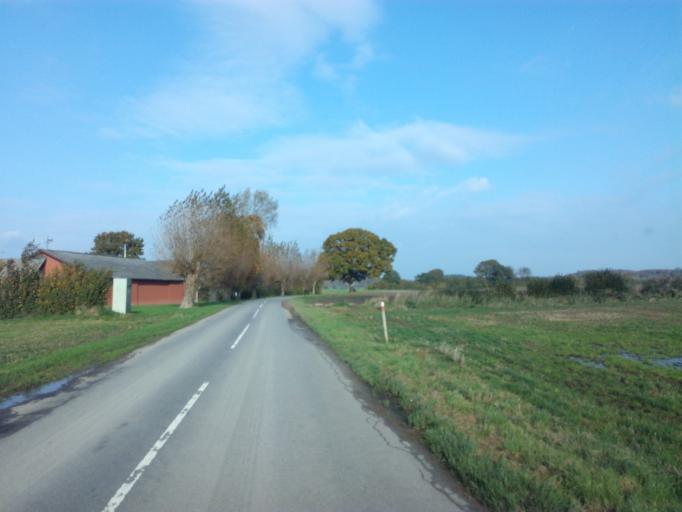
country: DK
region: South Denmark
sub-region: Vejle Kommune
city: Brejning
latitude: 55.6464
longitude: 9.6872
